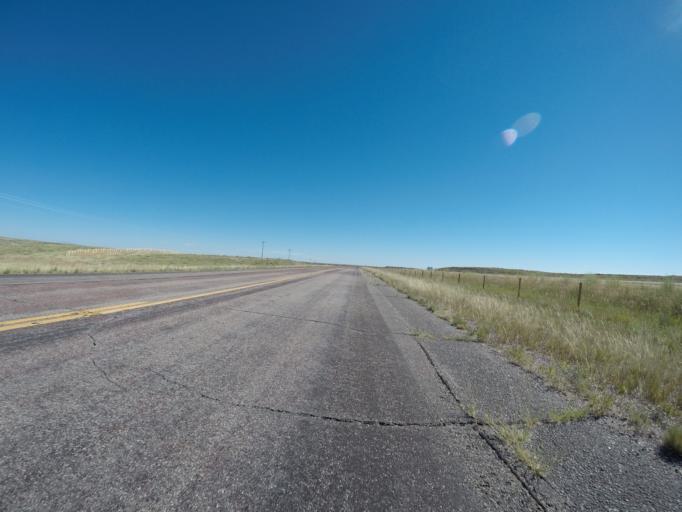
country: US
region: Wyoming
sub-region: Platte County
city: Wheatland
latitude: 41.6801
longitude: -104.8341
